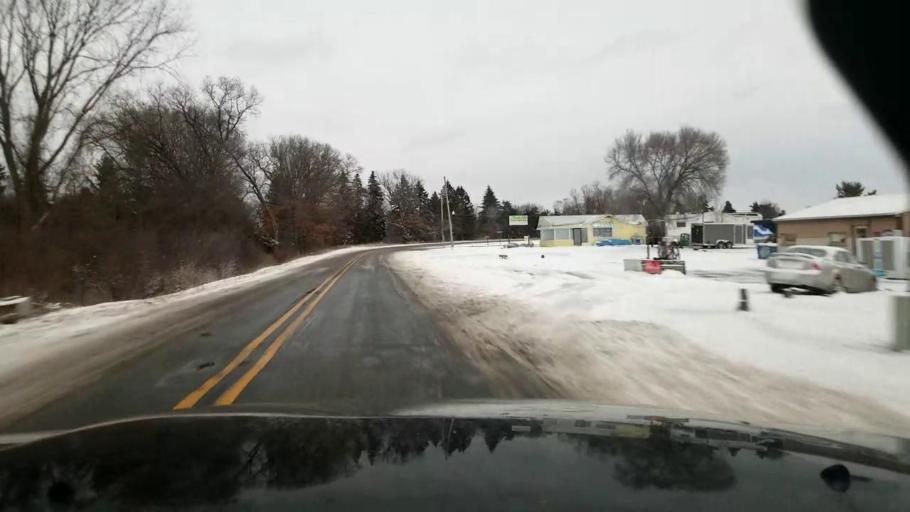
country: US
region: Michigan
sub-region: Jackson County
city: Vandercook Lake
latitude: 42.0967
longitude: -84.4770
